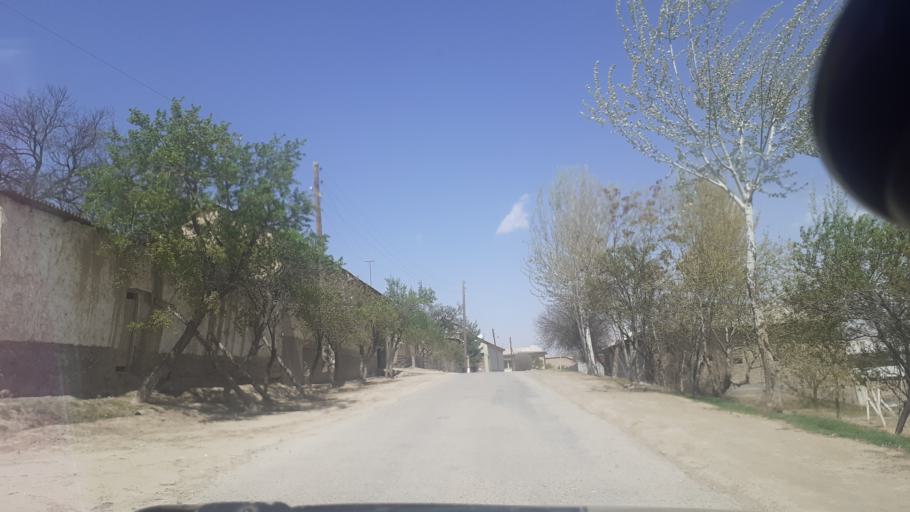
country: UZ
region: Namangan
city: Namangan
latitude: 41.0952
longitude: 71.6607
